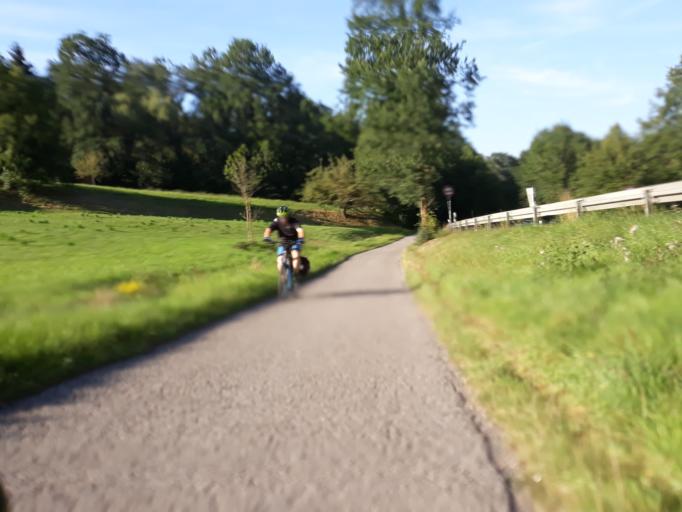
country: DE
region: Baden-Wuerttemberg
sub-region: Regierungsbezirk Stuttgart
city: Schonaich
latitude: 48.6503
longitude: 9.0486
